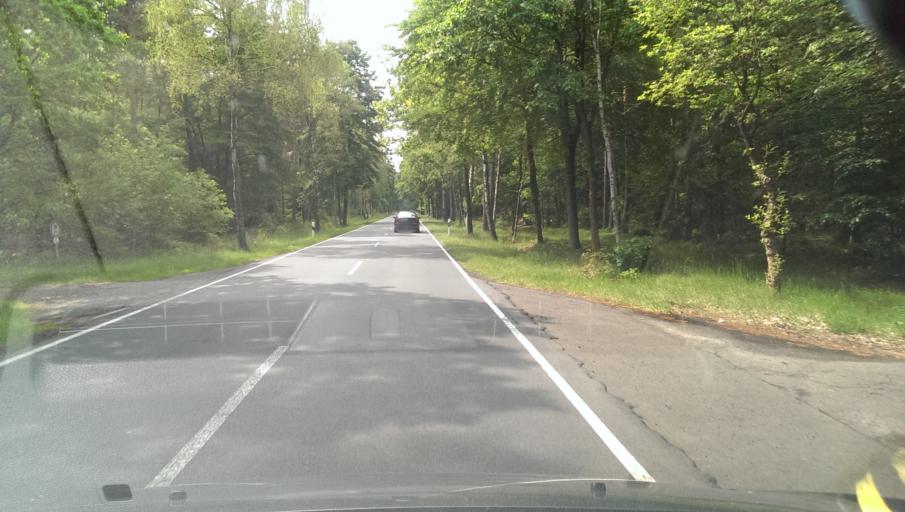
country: DE
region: Lower Saxony
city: Sprakensehl
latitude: 52.7863
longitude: 10.4023
